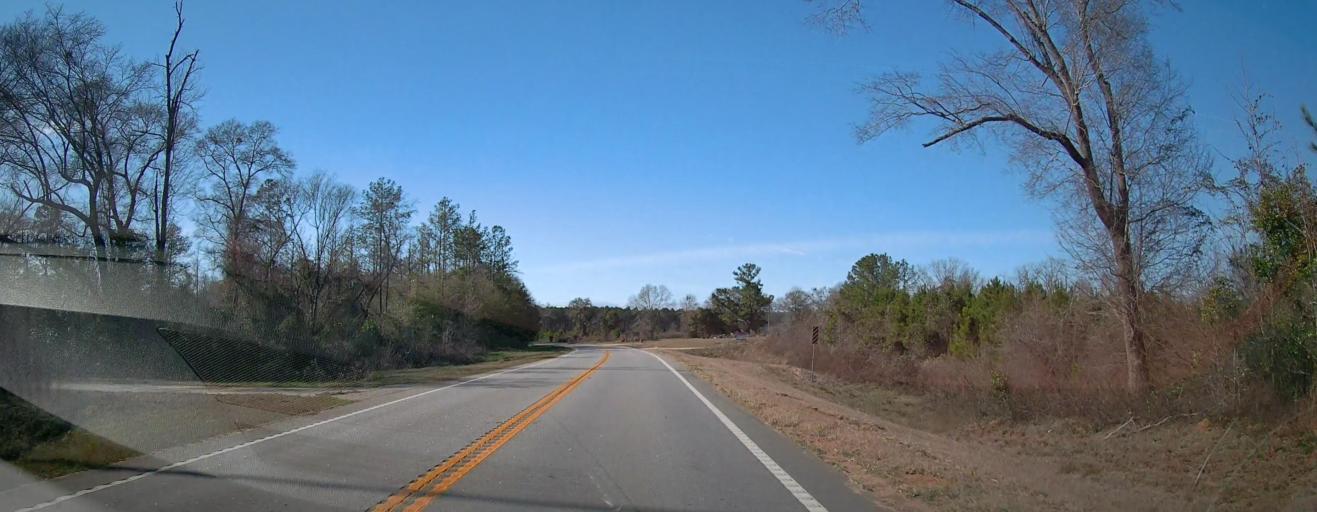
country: US
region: Georgia
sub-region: Macon County
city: Oglethorpe
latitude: 32.3488
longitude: -84.1478
